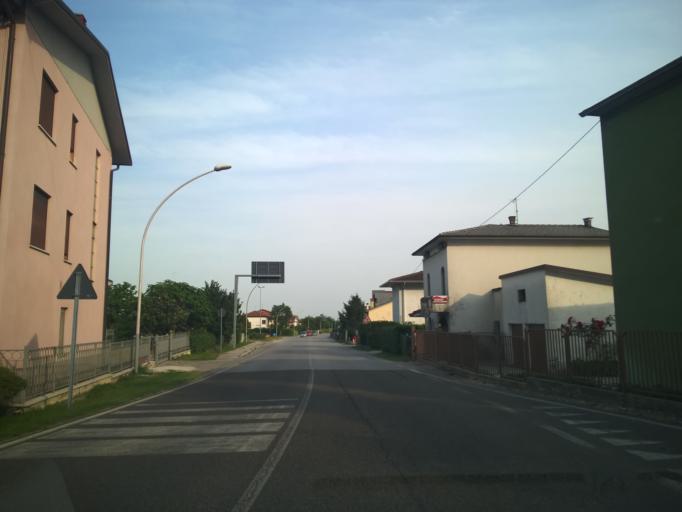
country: IT
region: Veneto
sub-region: Provincia di Vicenza
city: Piovene Rocchette
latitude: 45.7500
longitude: 11.4301
